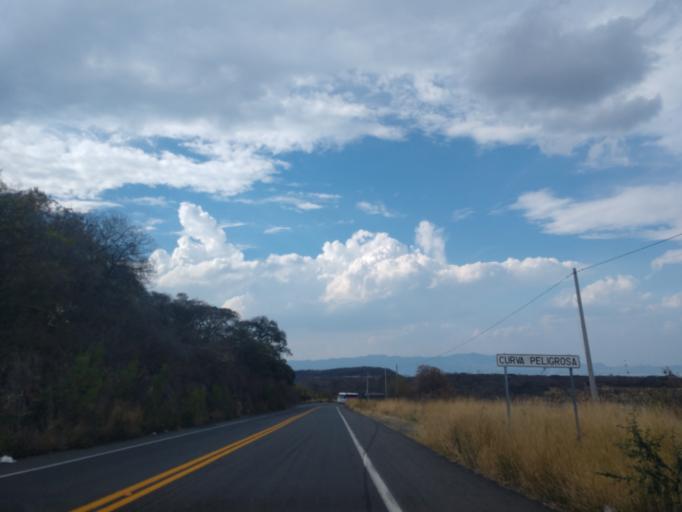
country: MX
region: Jalisco
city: La Manzanilla de la Paz
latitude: 20.1170
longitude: -103.1653
